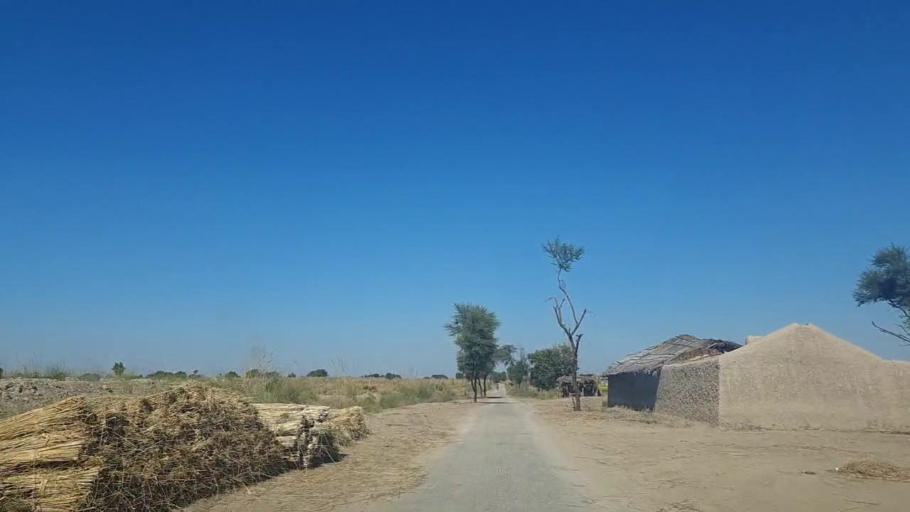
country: PK
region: Sindh
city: Khadro
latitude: 26.2114
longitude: 68.8600
